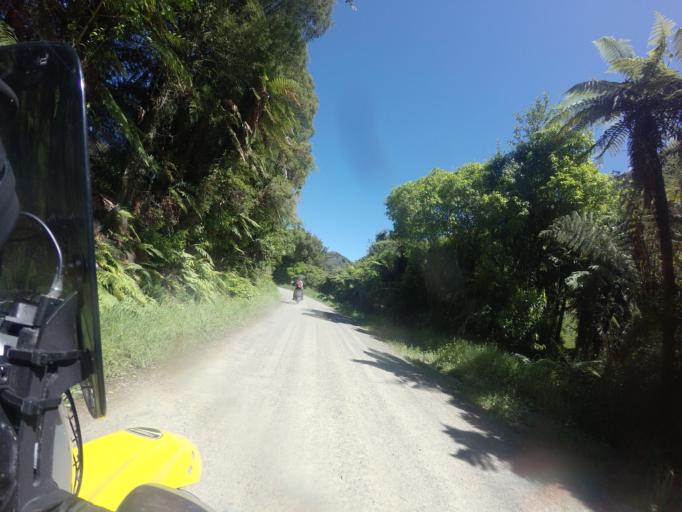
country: NZ
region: Bay of Plenty
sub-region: Opotiki District
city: Opotiki
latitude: -38.2810
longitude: 177.3403
